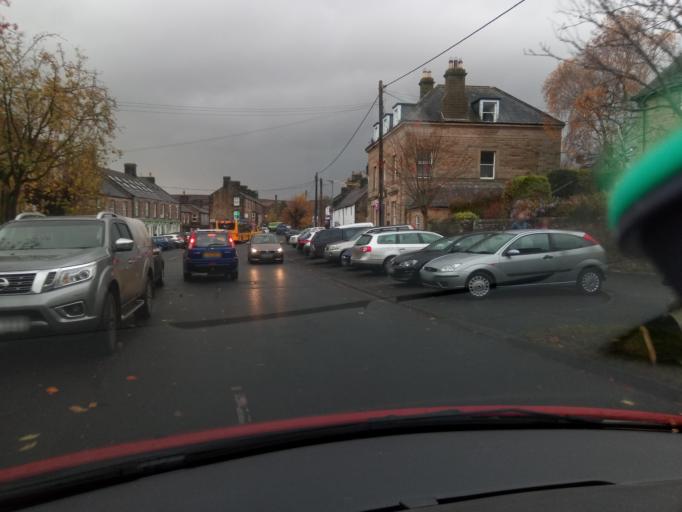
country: GB
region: England
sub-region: Northumberland
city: Birtley
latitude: 55.1449
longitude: -2.2535
